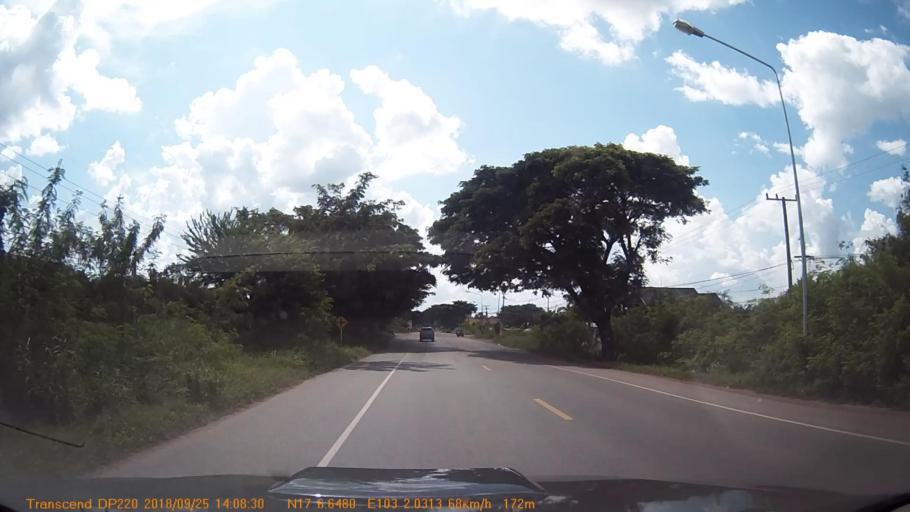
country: TH
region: Changwat Udon Thani
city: Kumphawapi
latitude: 17.1108
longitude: 103.0336
